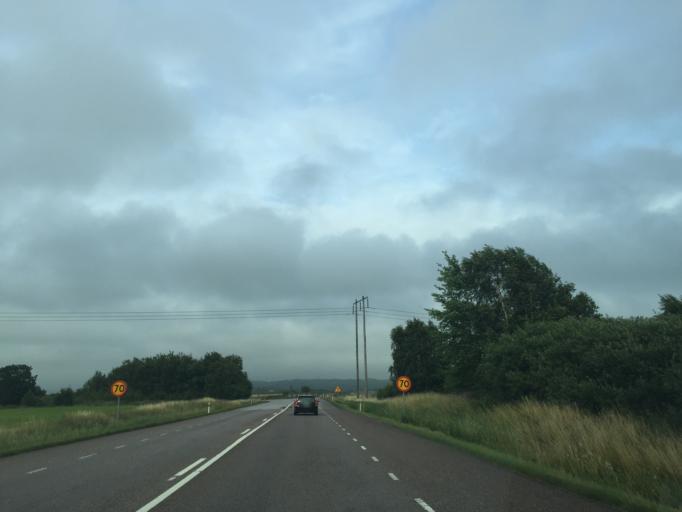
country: SE
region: Halland
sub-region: Falkenbergs Kommun
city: Falkenberg
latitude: 56.8830
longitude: 12.5916
